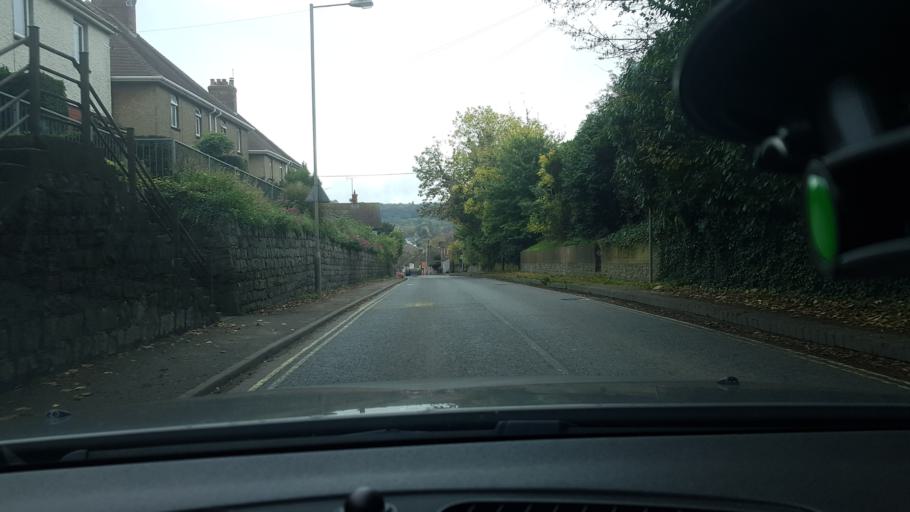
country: GB
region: England
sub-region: Wiltshire
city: Marlborough
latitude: 51.4248
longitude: -1.7304
